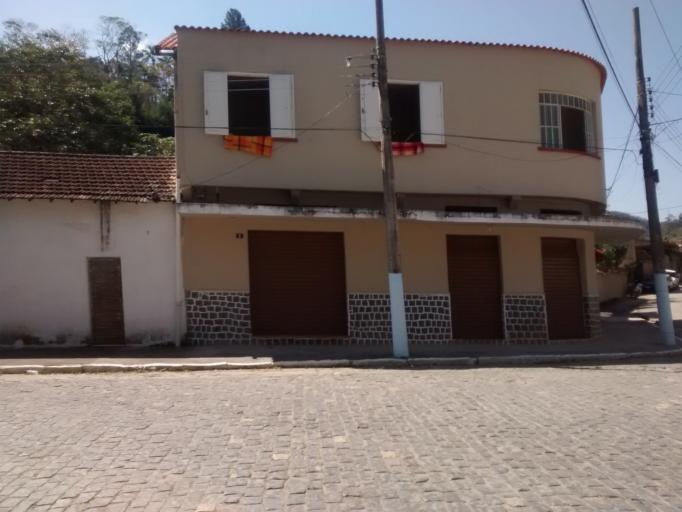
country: BR
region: Rio de Janeiro
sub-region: Vassouras
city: Vassouras
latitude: -22.4737
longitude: -43.5828
